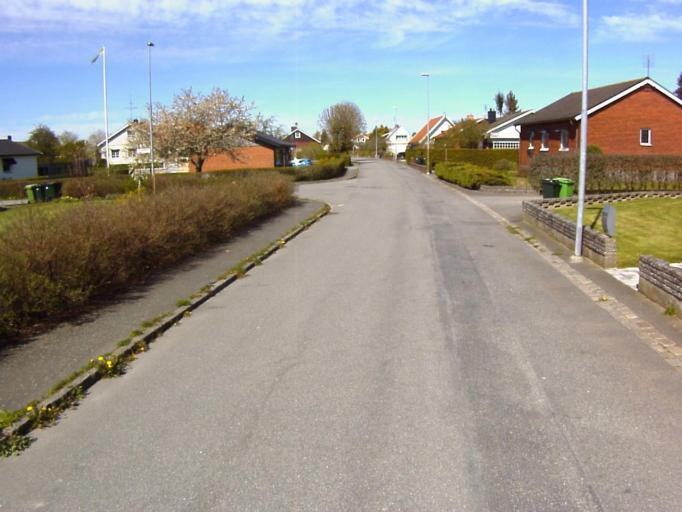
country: SE
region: Skane
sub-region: Kristianstads Kommun
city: Kristianstad
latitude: 56.0084
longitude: 14.1539
